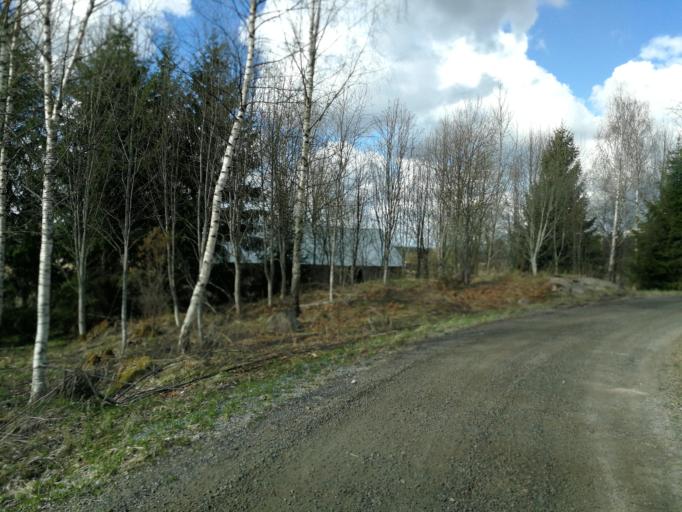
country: FI
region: Uusimaa
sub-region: Raaseporin
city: Inga
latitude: 60.1015
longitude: 23.9784
